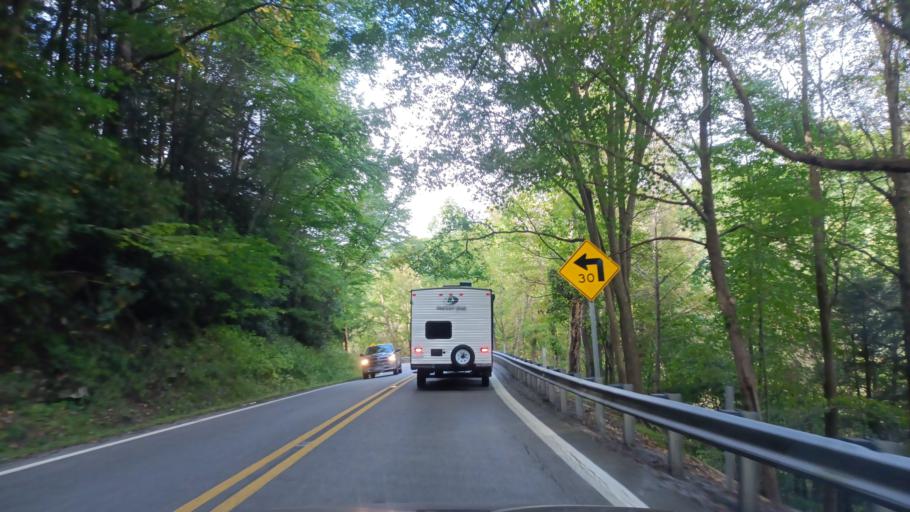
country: US
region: West Virginia
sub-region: Preston County
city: Terra Alta
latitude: 39.2958
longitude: -79.6218
